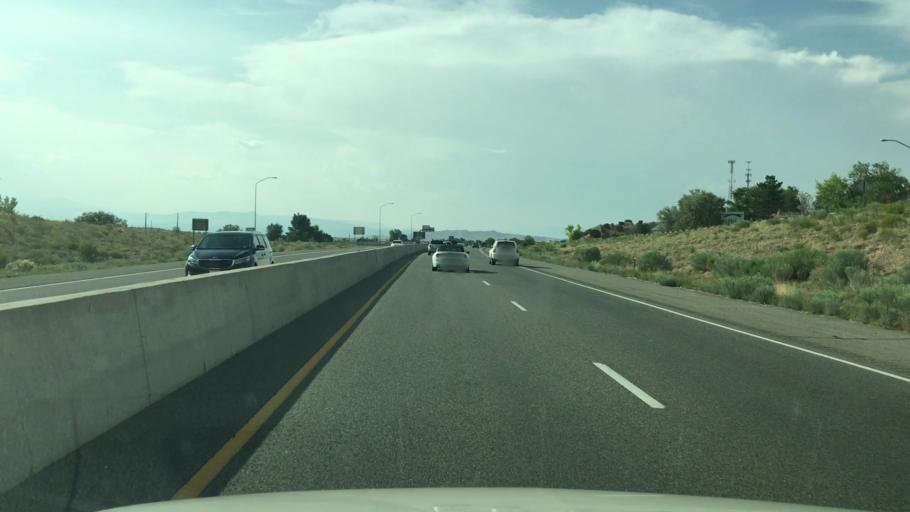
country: US
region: New Mexico
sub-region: Santa Fe County
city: Nambe
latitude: 35.8414
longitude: -105.9900
